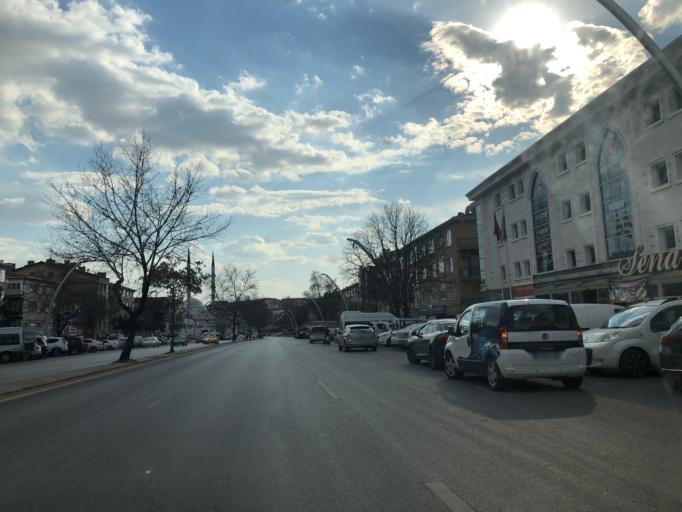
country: TR
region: Ankara
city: Mamak
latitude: 39.9872
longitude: 32.8653
